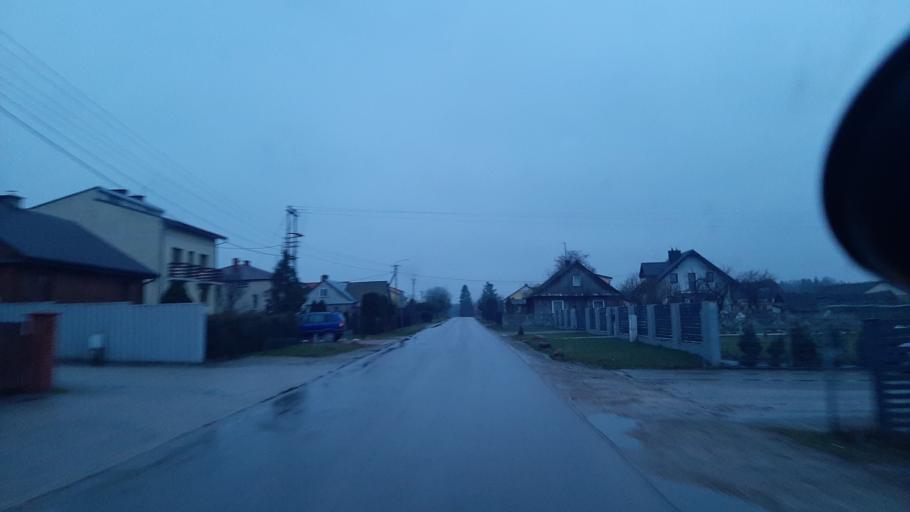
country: PL
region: Lublin Voivodeship
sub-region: Powiat lubartowski
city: Kamionka
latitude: 51.4043
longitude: 22.4148
